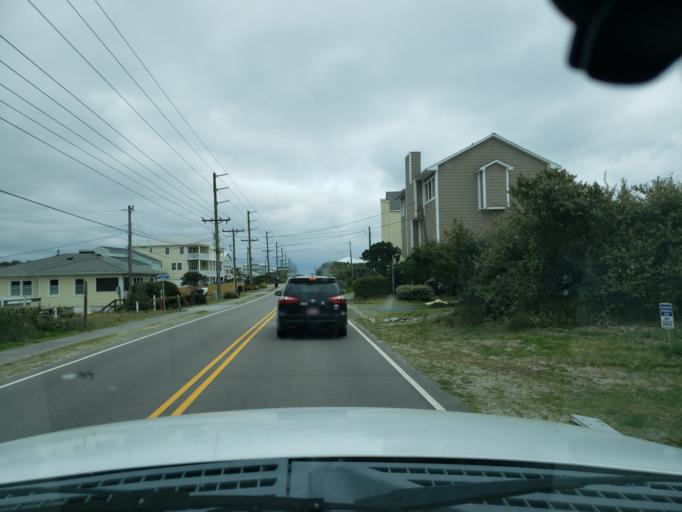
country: US
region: North Carolina
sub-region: Pender County
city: Surf City
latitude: 34.3907
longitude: -77.5963
